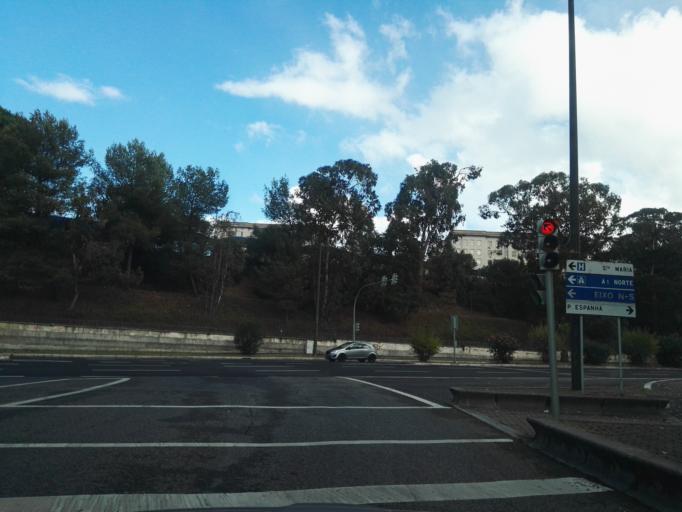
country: PT
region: Lisbon
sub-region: Odivelas
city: Pontinha
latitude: 38.7481
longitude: -9.1643
